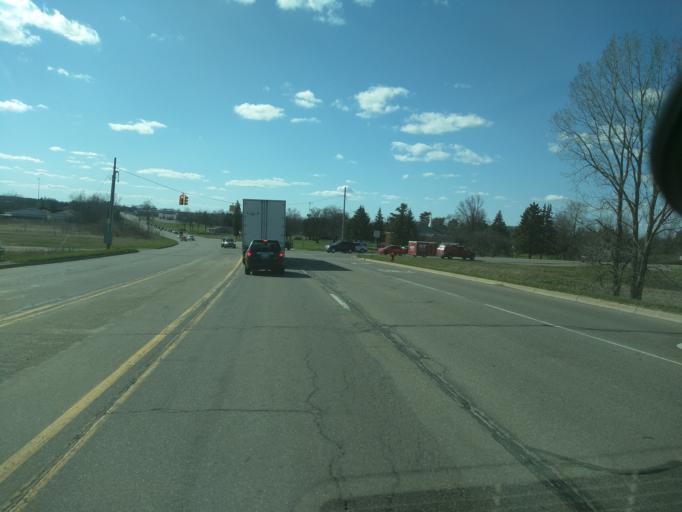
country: US
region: Michigan
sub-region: Ingham County
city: Edgemont Park
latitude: 42.7723
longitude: -84.6068
